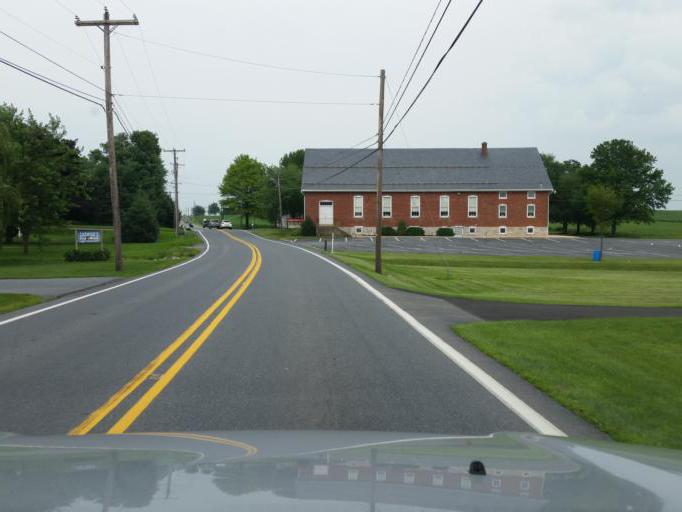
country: US
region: Pennsylvania
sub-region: Lancaster County
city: Salunga
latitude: 40.1294
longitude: -76.4441
